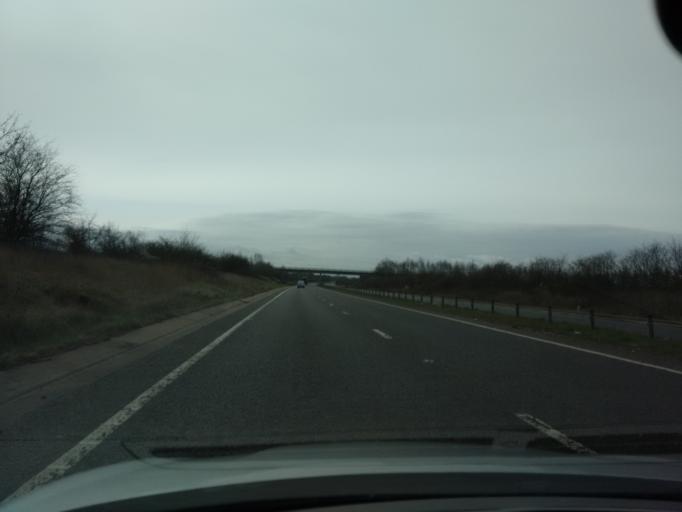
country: GB
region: England
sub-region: Warwickshire
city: Bidford-on-avon
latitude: 52.1803
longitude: -1.8789
